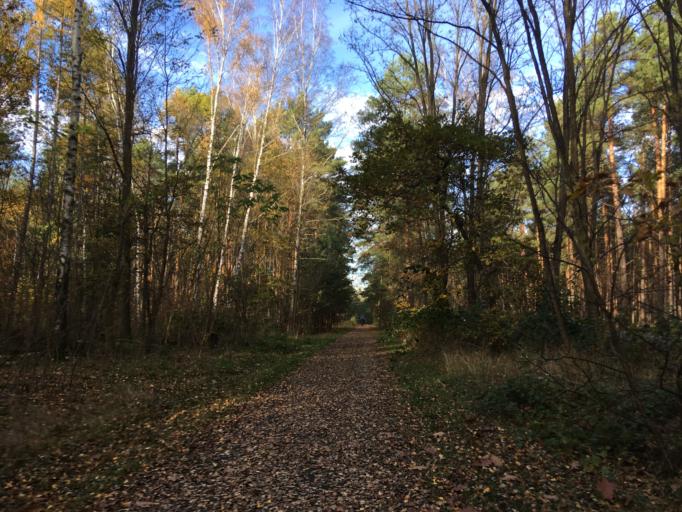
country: DE
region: Brandenburg
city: Gross Koris
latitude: 52.1572
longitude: 13.6726
